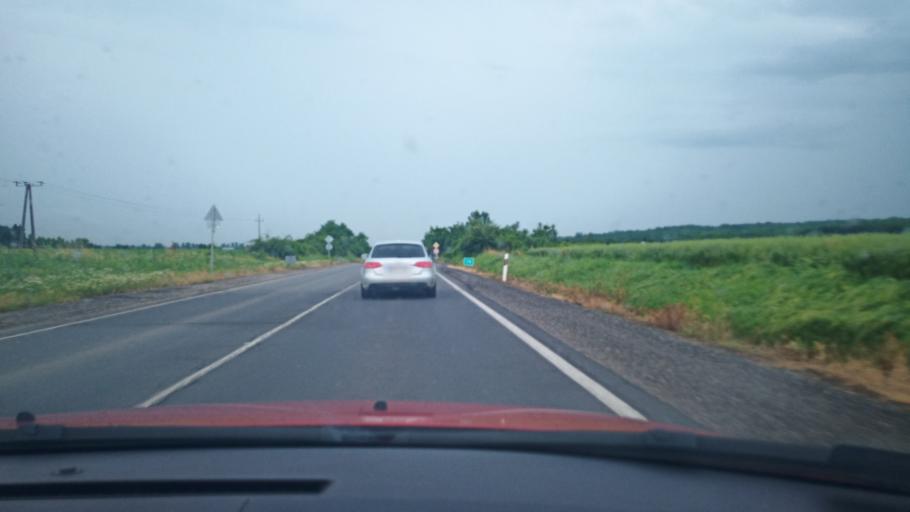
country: HU
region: Borsod-Abauj-Zemplen
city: Malyi
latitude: 48.0407
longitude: 20.8047
